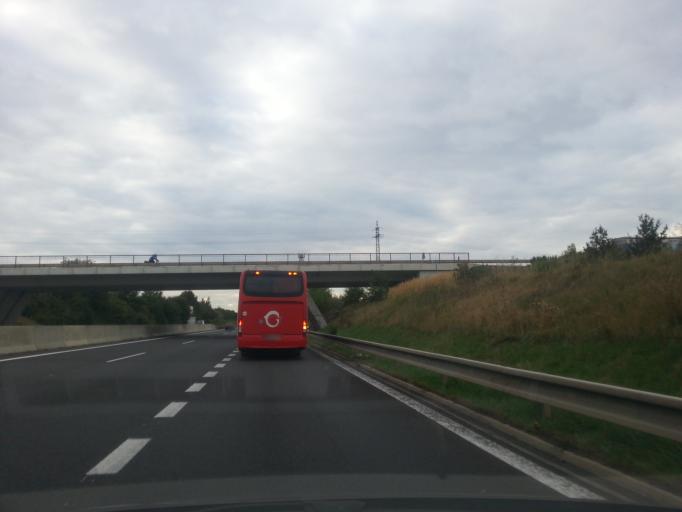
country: CZ
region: Central Bohemia
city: Unhost'
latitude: 50.1014
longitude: 14.1406
